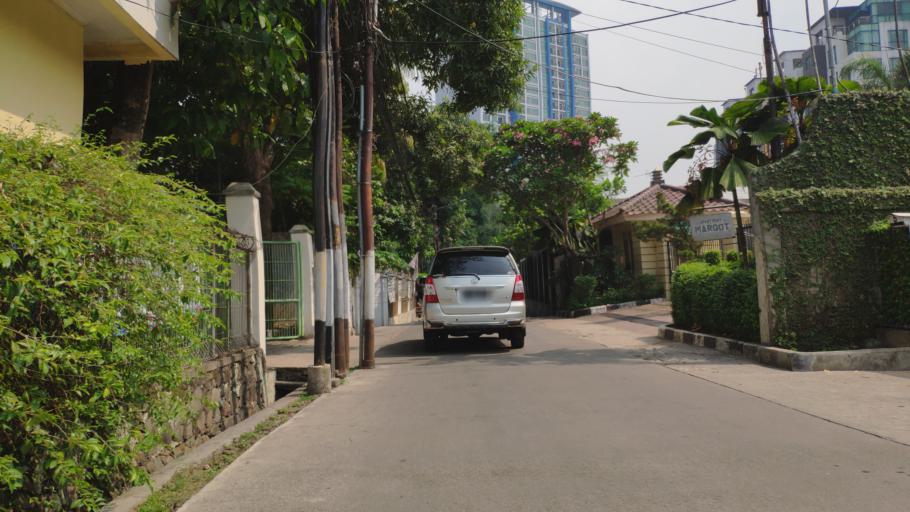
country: ID
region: Banten
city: South Tangerang
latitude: -6.2846
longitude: 106.7902
